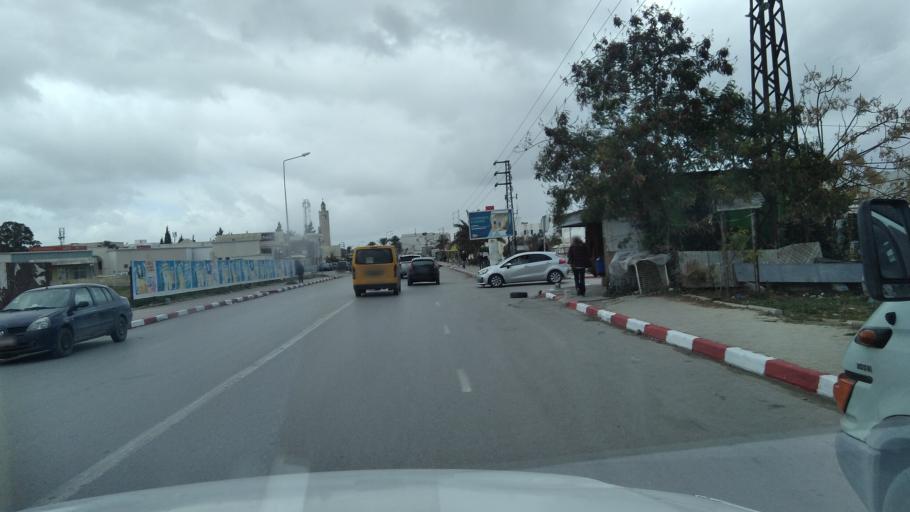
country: TN
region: Bin 'Arus
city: Ben Arous
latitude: 36.7498
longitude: 10.2274
